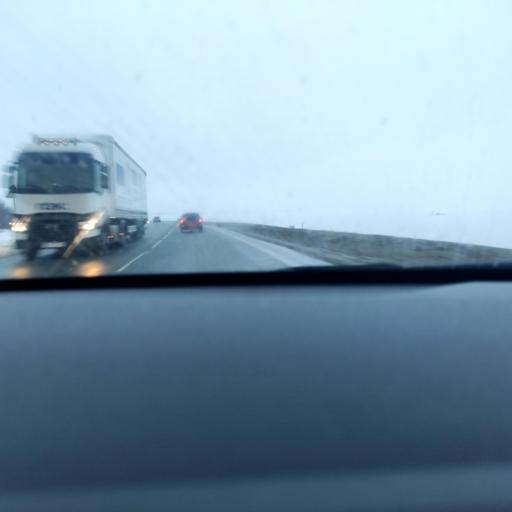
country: RU
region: Tatarstan
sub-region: Alekseyevskiy Rayon
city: Alekseyevskoye
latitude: 55.3149
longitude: 50.2774
